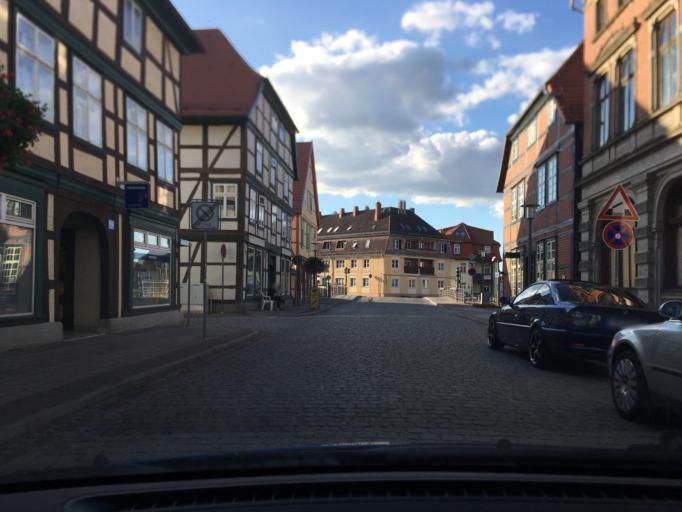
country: DE
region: Mecklenburg-Vorpommern
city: Grabow
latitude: 53.2796
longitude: 11.5631
